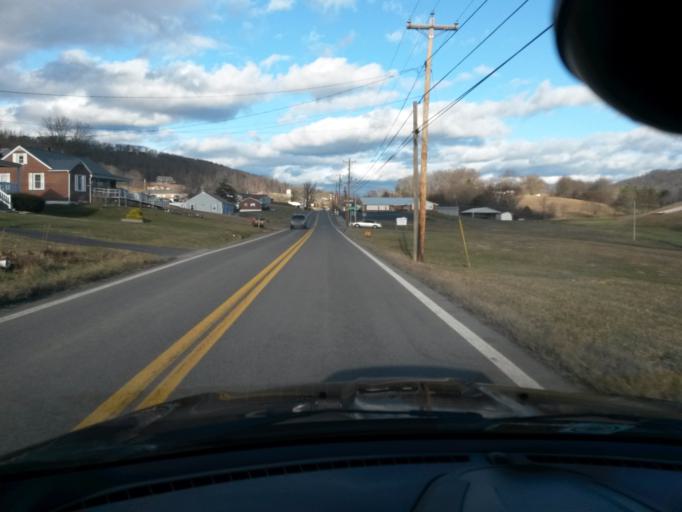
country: US
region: Virginia
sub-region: Giles County
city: Pearisburg
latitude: 37.4058
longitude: -80.7583
